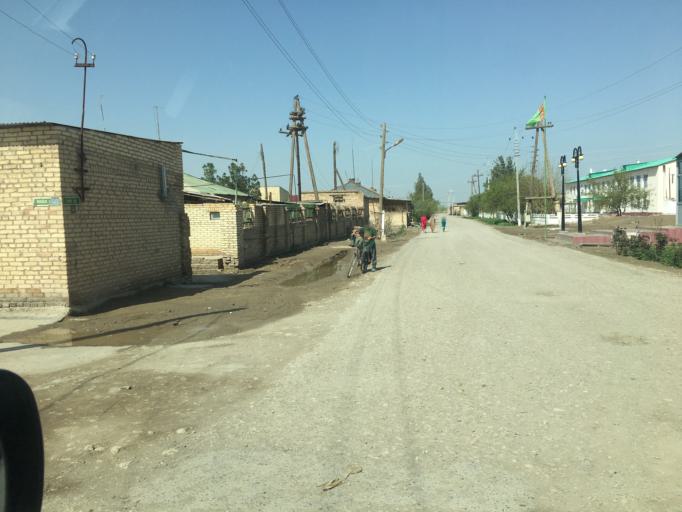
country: TM
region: Lebap
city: Turkmenabat
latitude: 38.9636
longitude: 63.6514
